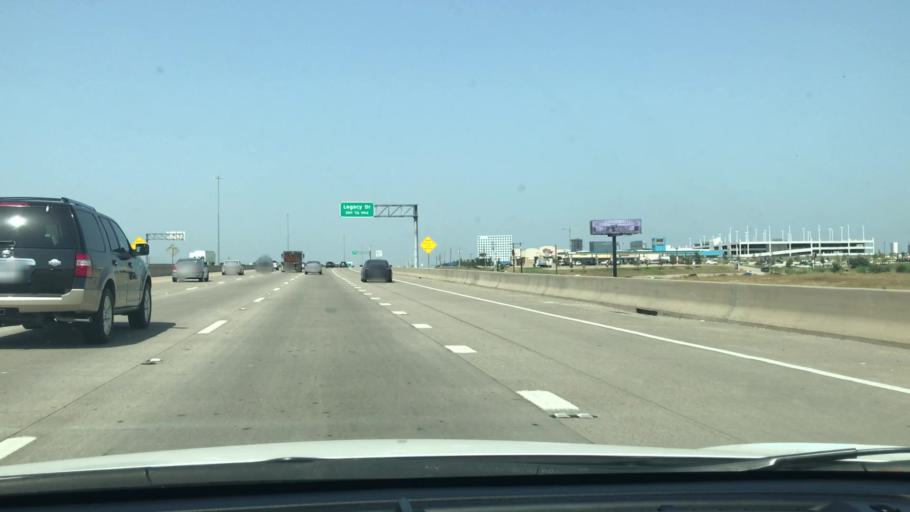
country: US
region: Texas
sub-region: Denton County
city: The Colony
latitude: 33.0813
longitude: -96.8547
